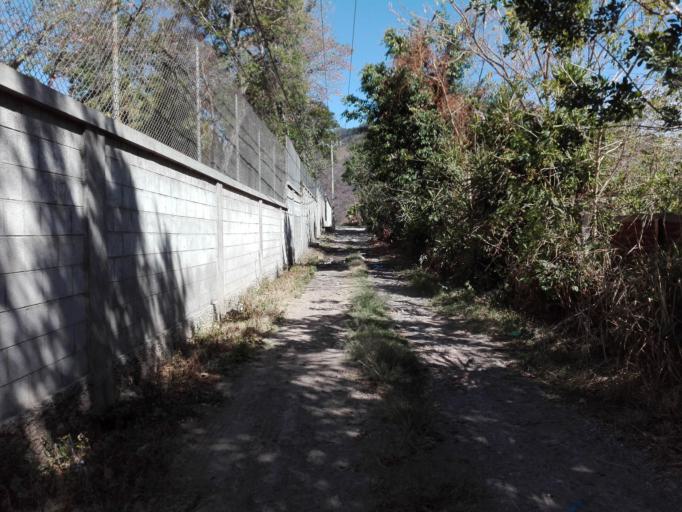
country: GT
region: Guatemala
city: Amatitlan
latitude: 14.4770
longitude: -90.5985
